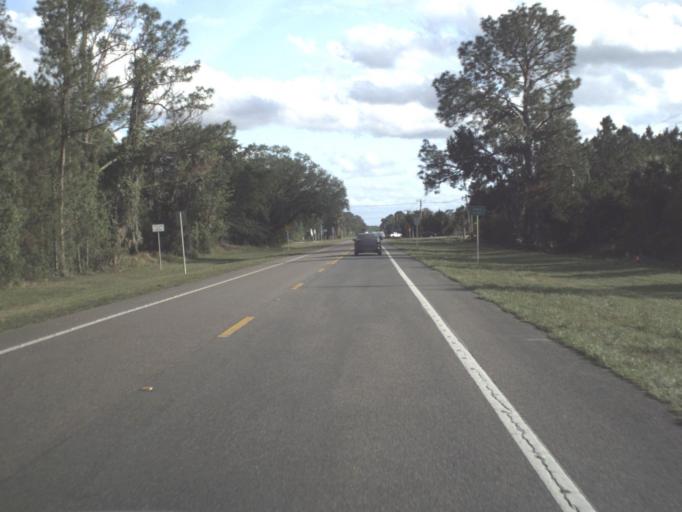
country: US
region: Florida
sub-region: Flagler County
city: Bunnell
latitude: 29.3458
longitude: -81.3111
